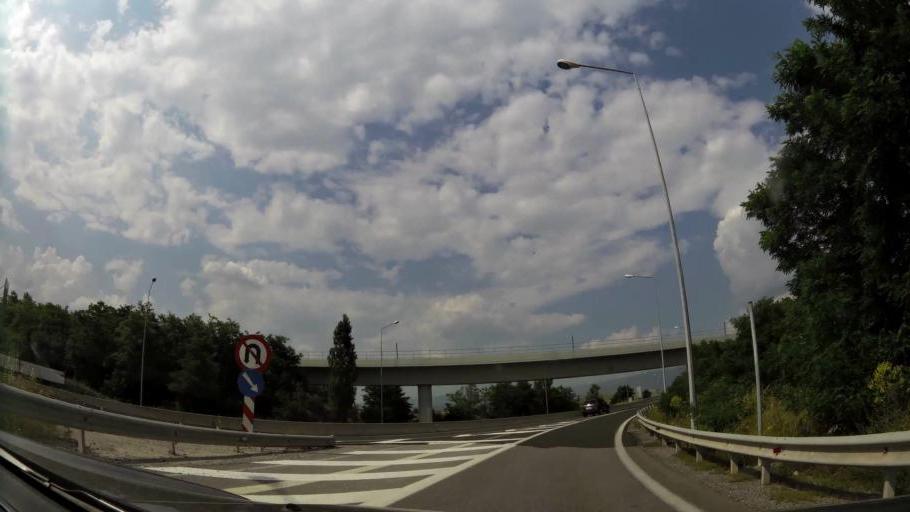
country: GR
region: West Macedonia
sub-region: Nomos Kozanis
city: Koila
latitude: 40.3499
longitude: 21.8082
